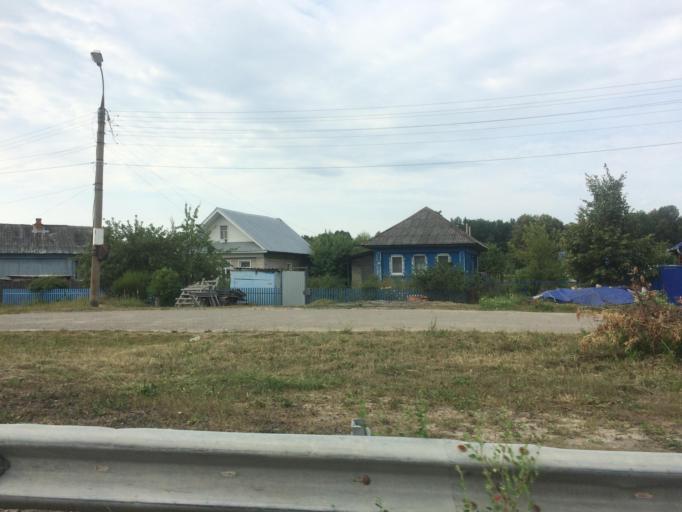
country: RU
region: Mariy-El
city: Yoshkar-Ola
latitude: 56.5557
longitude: 47.9842
